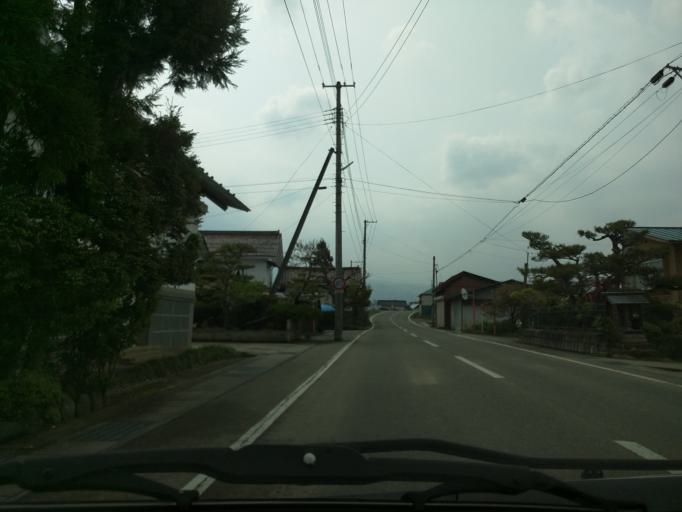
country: JP
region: Fukushima
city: Kitakata
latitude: 37.4412
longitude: 139.8543
